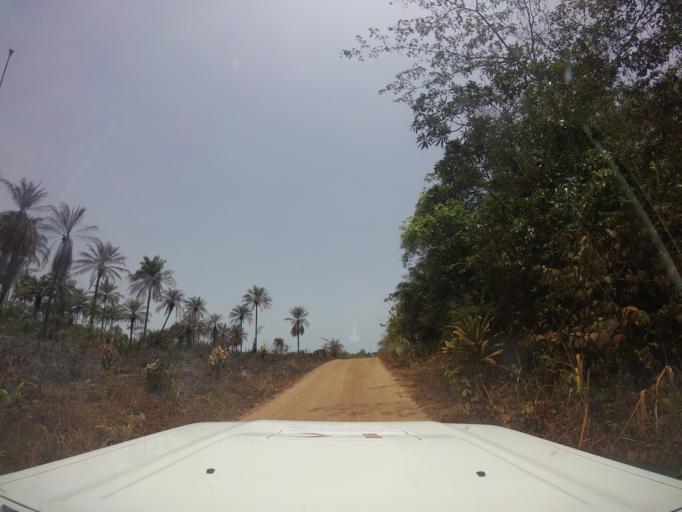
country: LR
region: Grand Cape Mount
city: Robertsport
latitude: 6.9601
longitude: -11.3180
